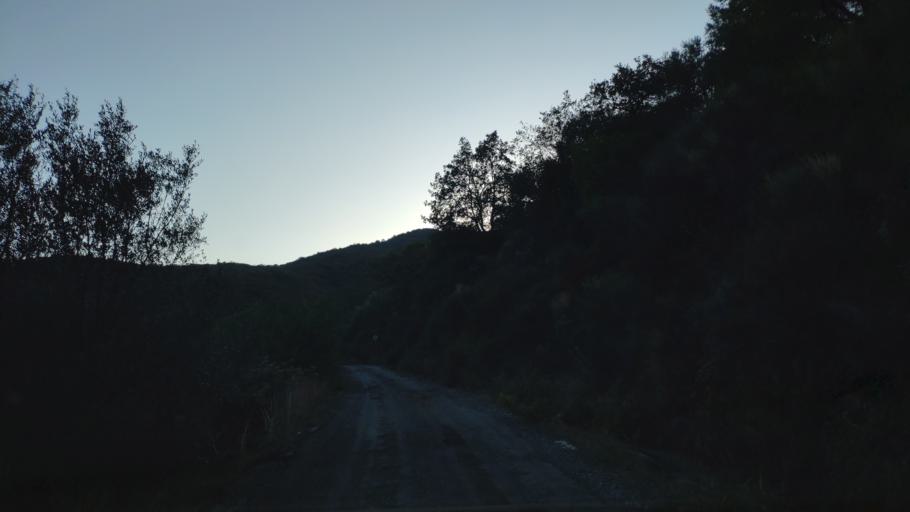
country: GR
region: Peloponnese
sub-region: Nomos Arkadias
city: Dimitsana
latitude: 37.5684
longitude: 22.0480
